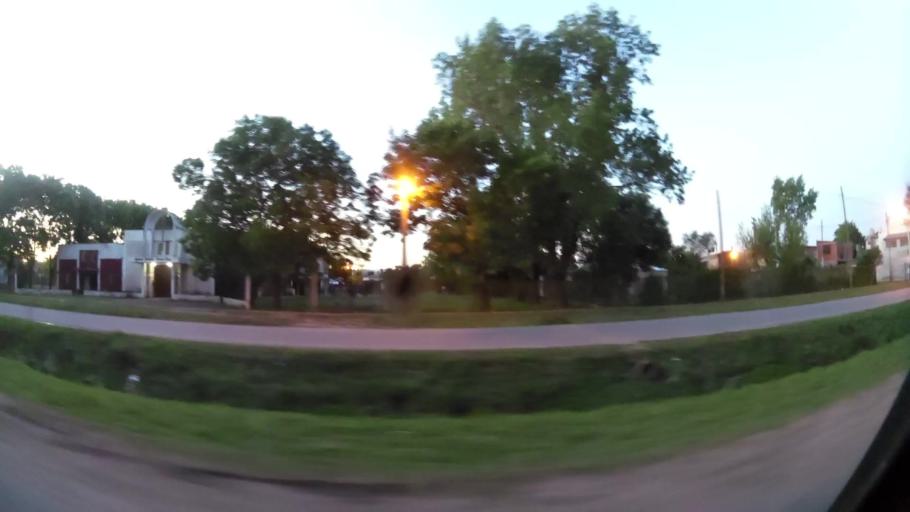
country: AR
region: Buenos Aires
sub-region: Partido de Almirante Brown
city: Adrogue
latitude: -34.7799
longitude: -58.3229
